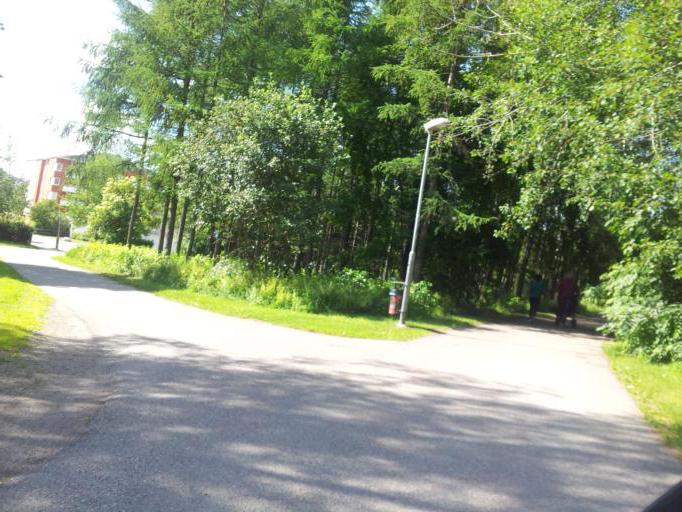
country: SE
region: Uppsala
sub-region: Uppsala Kommun
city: Uppsala
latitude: 59.8781
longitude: 17.6613
